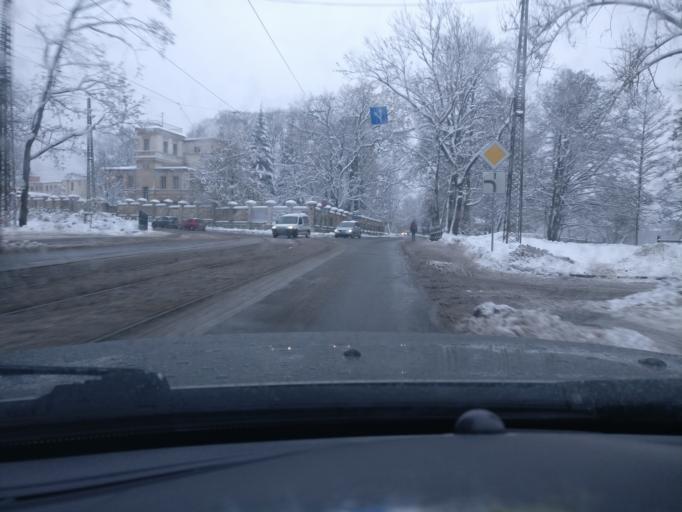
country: LV
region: Riga
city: Riga
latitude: 56.9322
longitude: 24.0826
